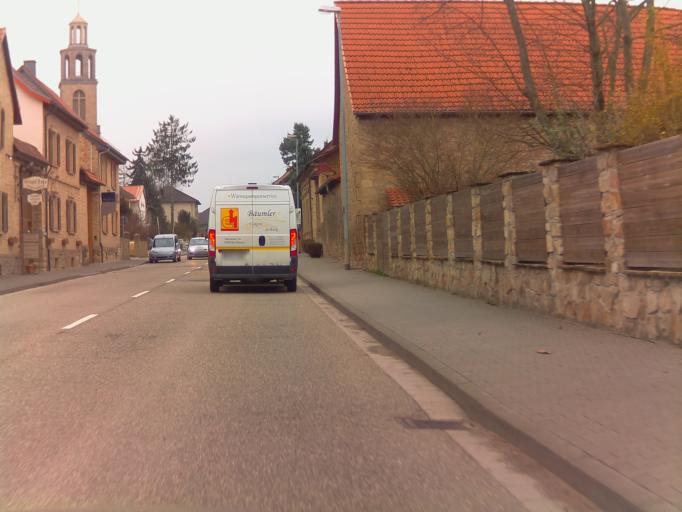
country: DE
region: Rheinland-Pfalz
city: Gau-Bickelheim
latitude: 49.8352
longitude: 8.0232
